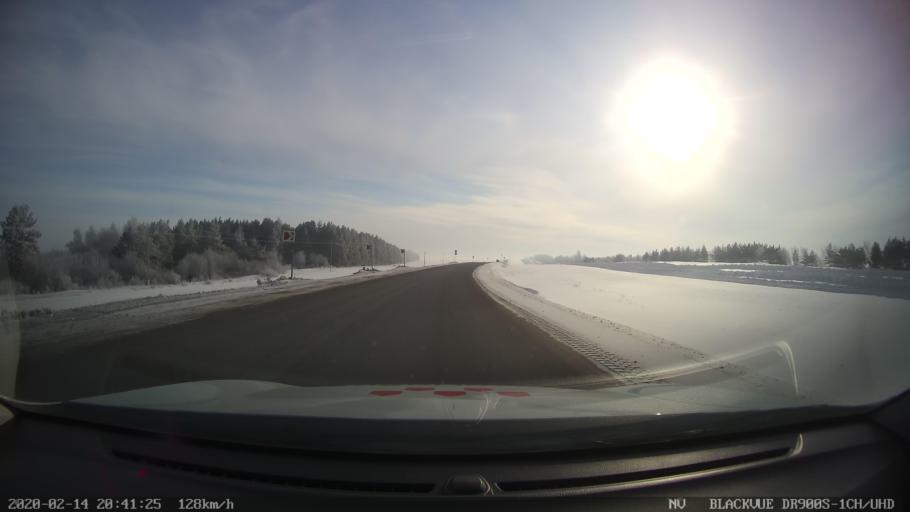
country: RU
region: Tatarstan
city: Kuybyshevskiy Zaton
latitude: 55.3306
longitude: 49.1193
